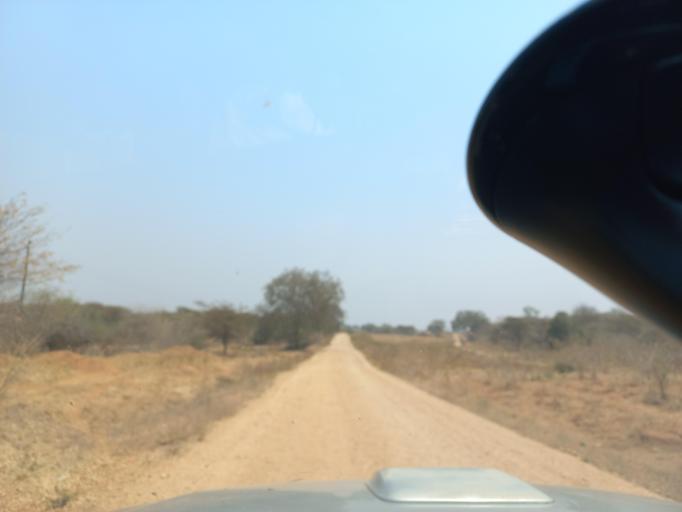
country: ZW
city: Chirundu
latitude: -15.9338
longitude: 28.8636
